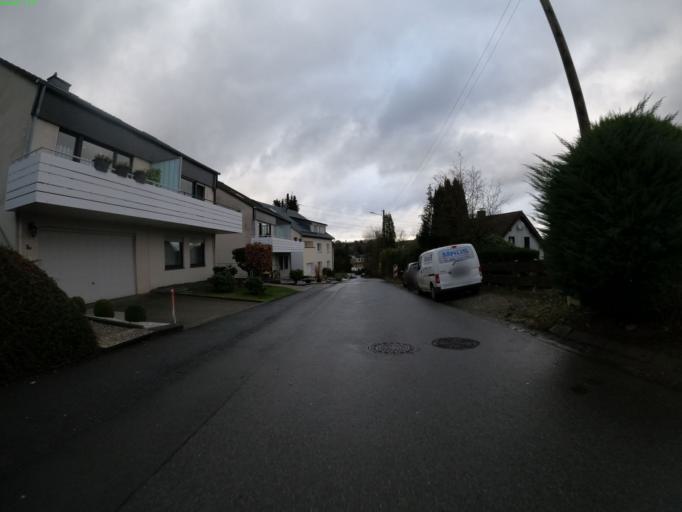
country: DE
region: North Rhine-Westphalia
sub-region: Regierungsbezirk Dusseldorf
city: Remscheid
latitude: 51.1844
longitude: 7.1383
